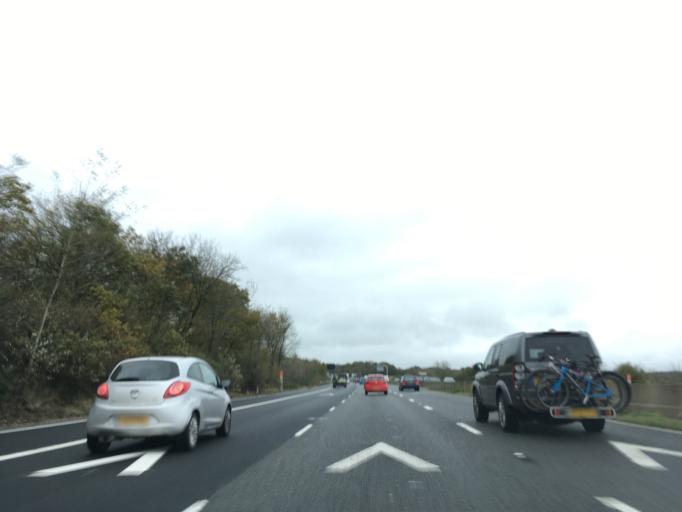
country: GB
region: England
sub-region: Wiltshire
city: Royal Wootton Bassett
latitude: 51.5528
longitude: -1.9250
